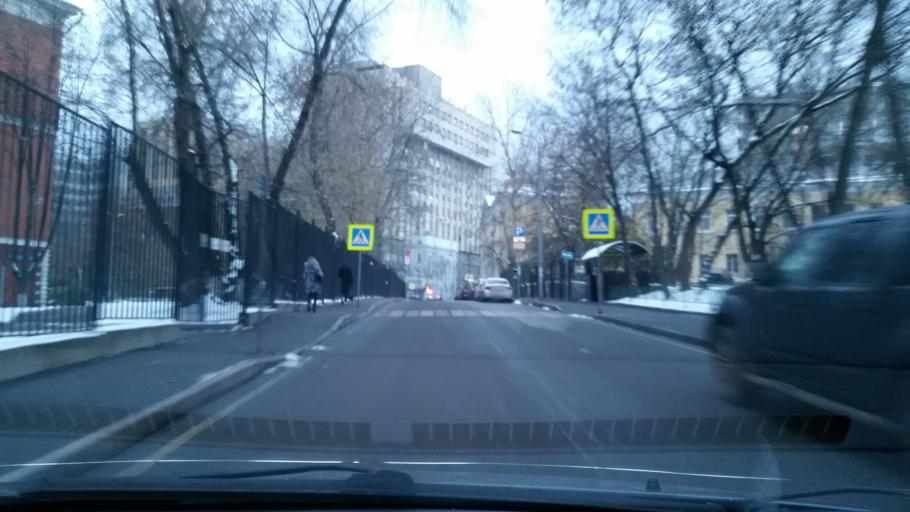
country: RU
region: Moscow
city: Luzhniki
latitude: 55.7307
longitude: 37.5609
